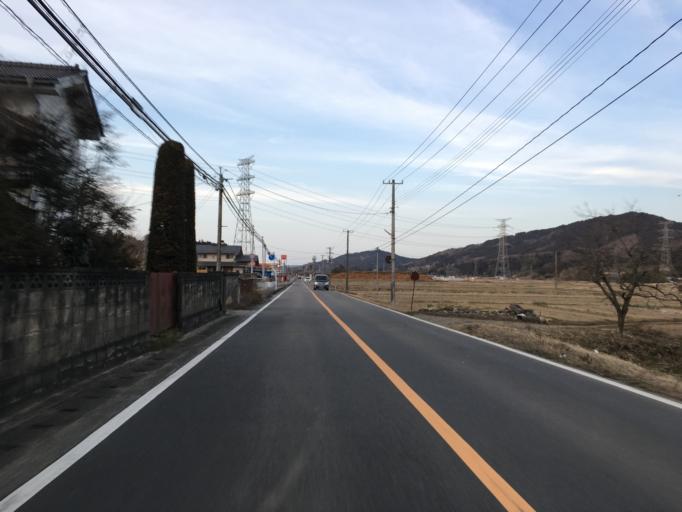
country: JP
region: Ibaraki
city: Daigo
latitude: 36.9232
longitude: 140.4079
